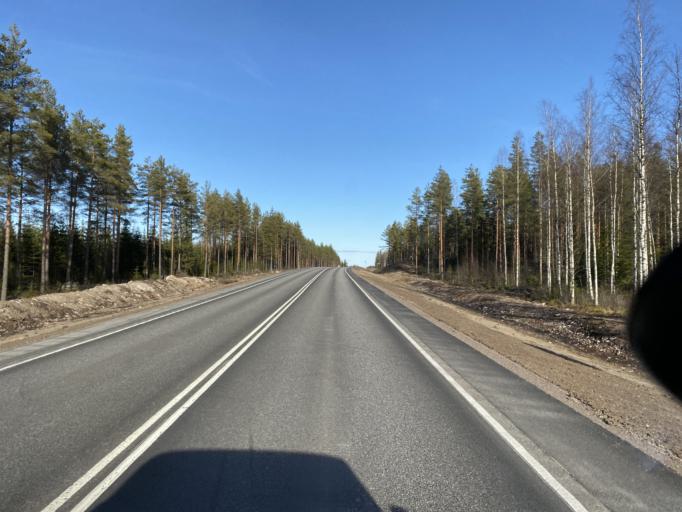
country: FI
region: Satakunta
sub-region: Pori
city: Kokemaeki
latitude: 61.1702
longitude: 22.4702
